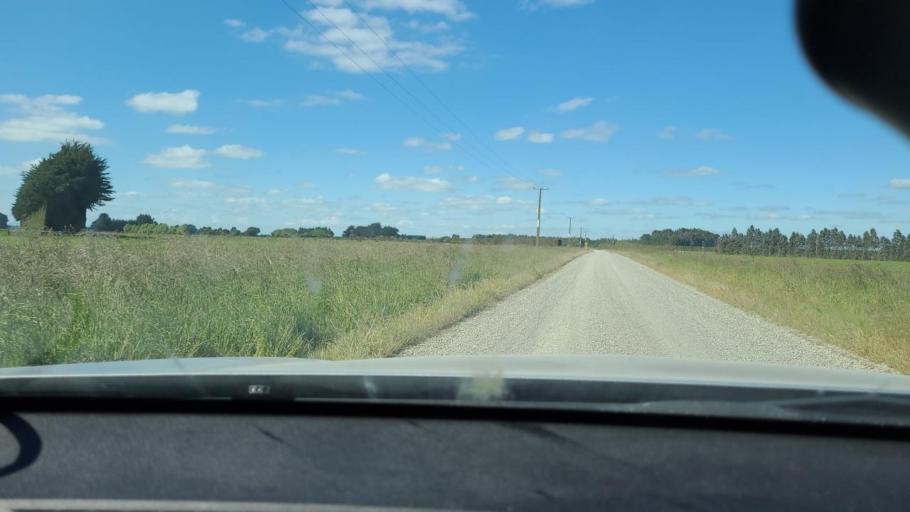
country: NZ
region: Southland
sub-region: Southland District
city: Riverton
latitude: -46.2735
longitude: 168.1654
